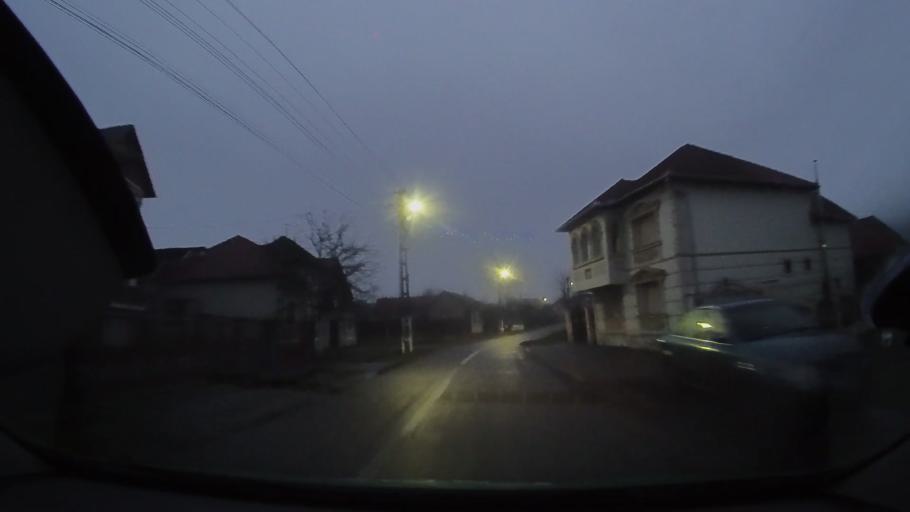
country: RO
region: Arad
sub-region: Comuna Archis
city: Archis
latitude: 46.4784
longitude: 22.0449
